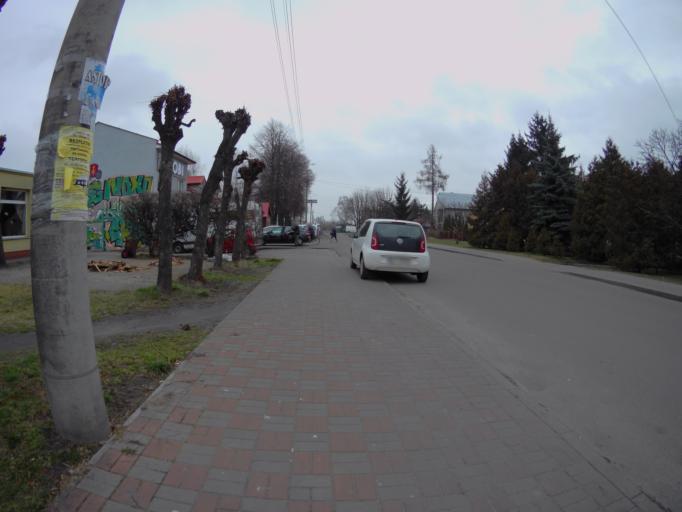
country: PL
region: Lublin Voivodeship
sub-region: Powiat bialski
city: Terespol
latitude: 52.0740
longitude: 23.6093
